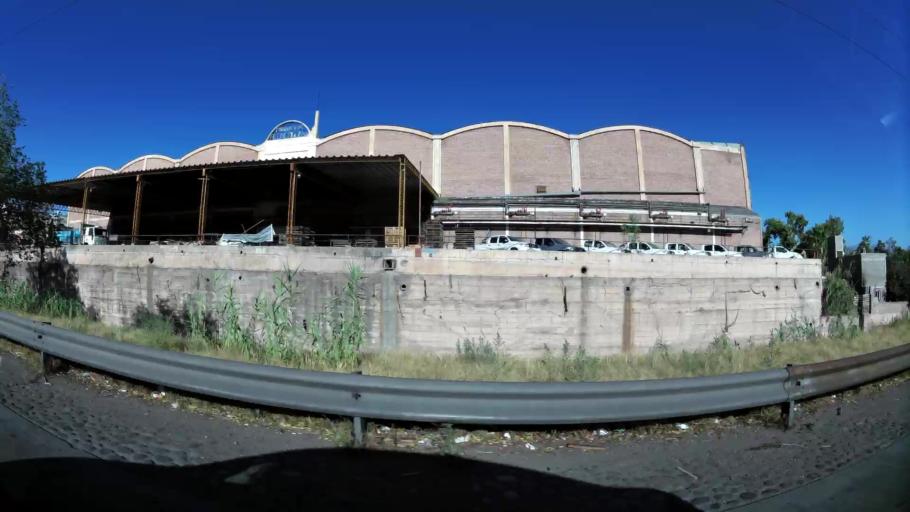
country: AR
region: Mendoza
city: Mendoza
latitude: -32.9068
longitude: -68.8380
